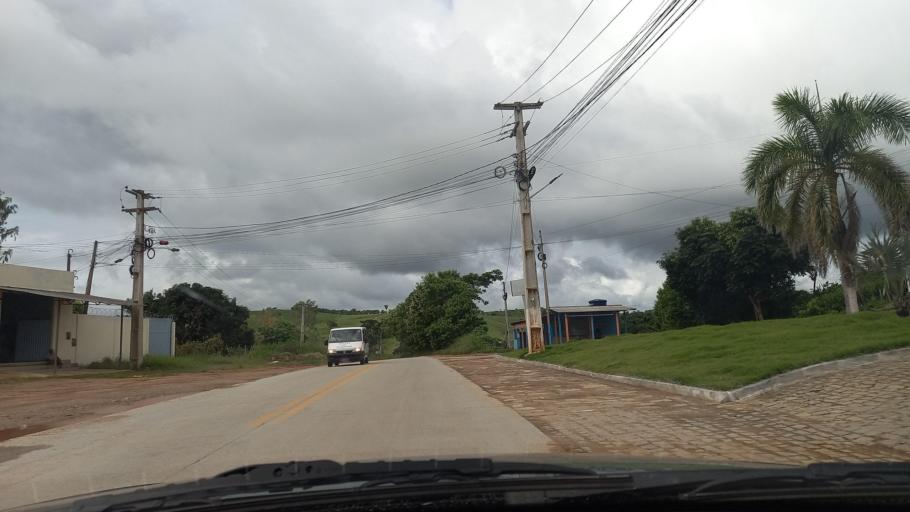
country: BR
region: Pernambuco
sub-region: Quipapa
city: Quipapa
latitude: -8.8114
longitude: -36.0111
